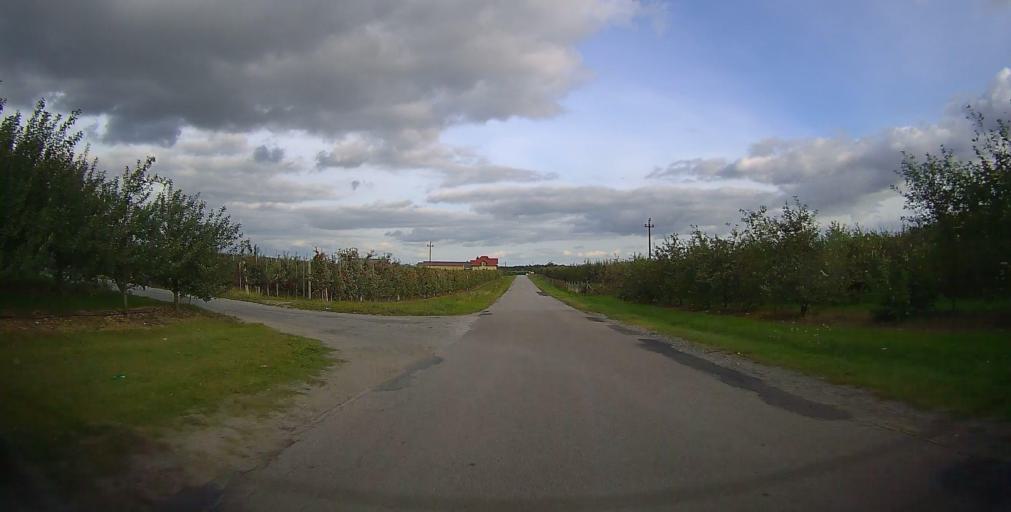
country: PL
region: Masovian Voivodeship
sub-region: Powiat grojecki
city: Goszczyn
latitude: 51.7574
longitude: 20.9135
